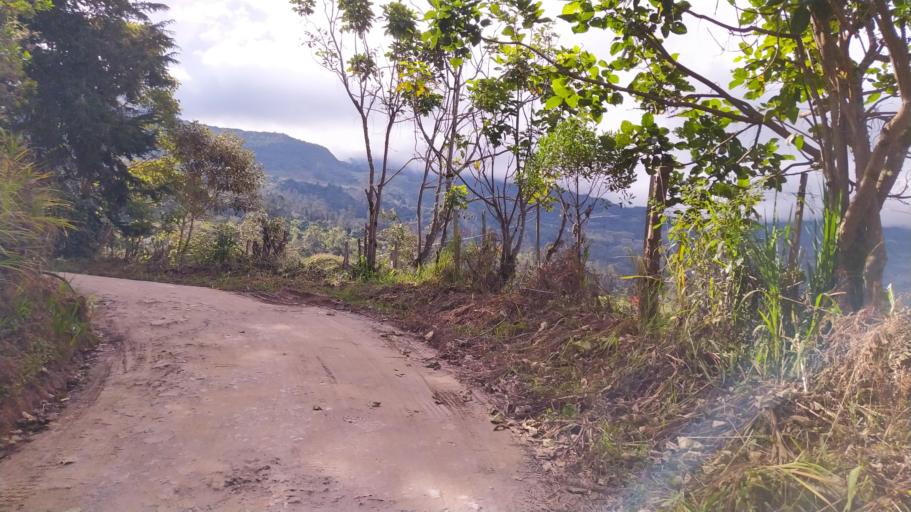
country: CO
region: Cundinamarca
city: Tenza
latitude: 5.0915
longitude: -73.4651
